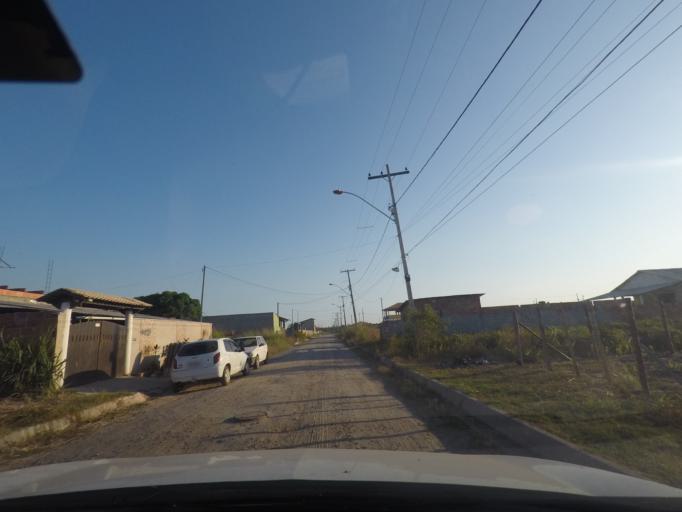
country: BR
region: Rio de Janeiro
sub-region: Marica
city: Marica
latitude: -22.9604
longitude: -42.9280
